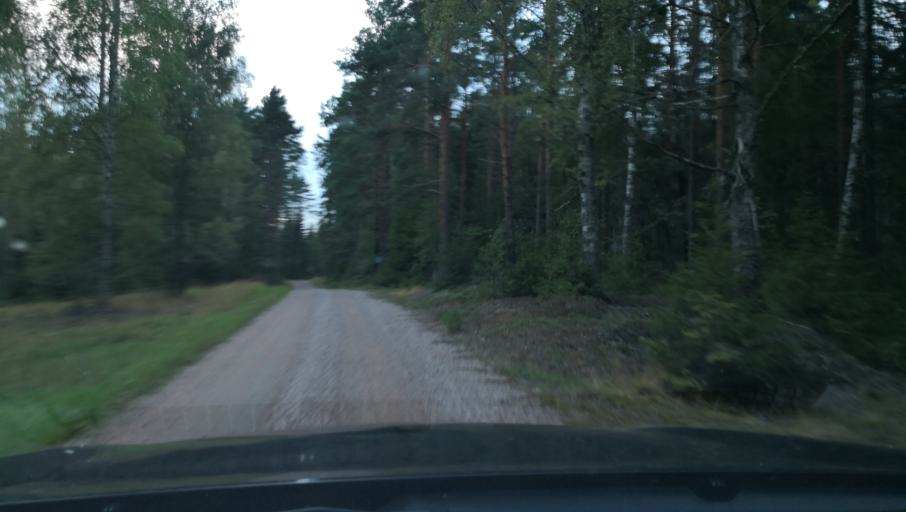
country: SE
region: Vaestmanland
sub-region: Arboga Kommun
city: Tyringe
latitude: 59.3553
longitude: 15.9987
